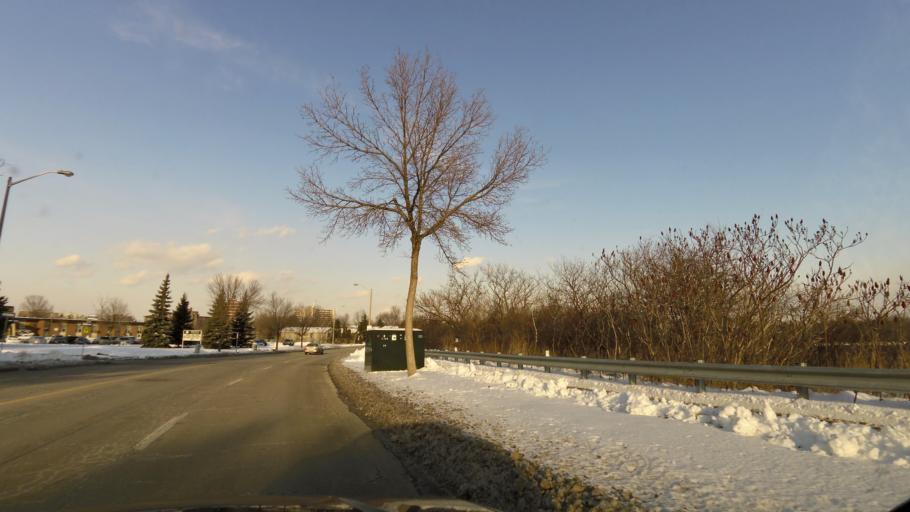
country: CA
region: Ontario
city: Etobicoke
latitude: 43.7336
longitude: -79.5828
